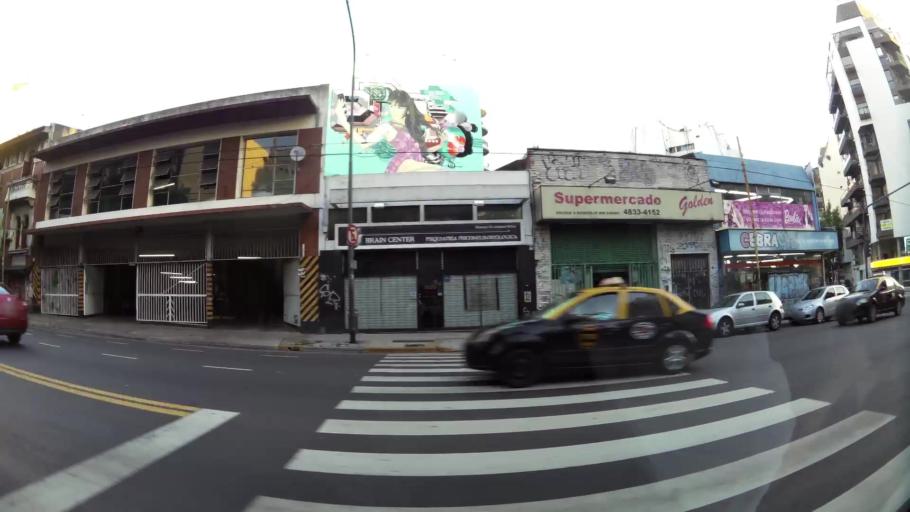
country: AR
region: Buenos Aires F.D.
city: Colegiales
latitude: -34.5891
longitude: -58.4222
